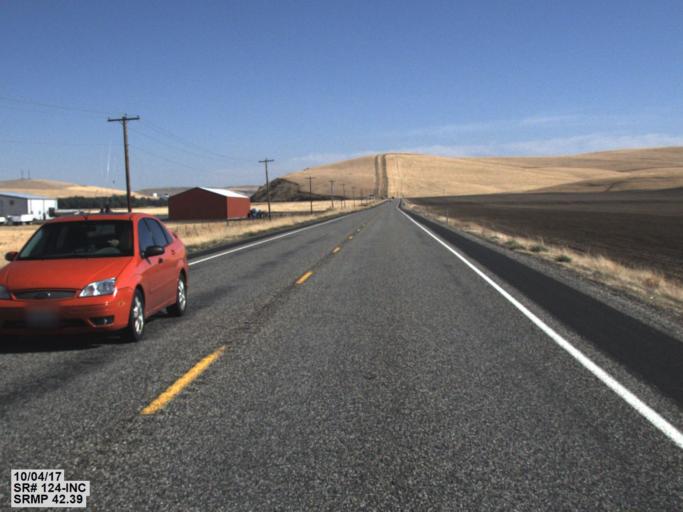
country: US
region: Washington
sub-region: Walla Walla County
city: Waitsburg
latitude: 46.2666
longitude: -118.2048
